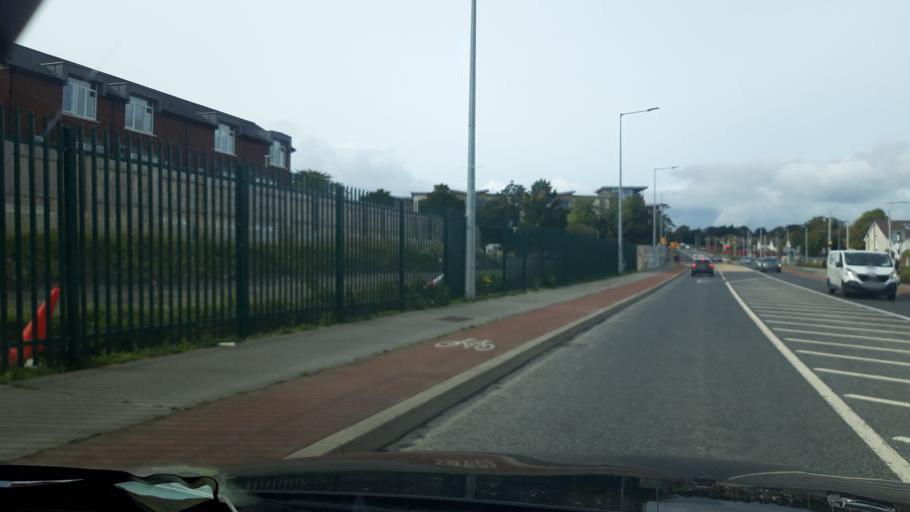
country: IE
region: Leinster
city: Sandyford
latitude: 53.2600
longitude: -6.2036
